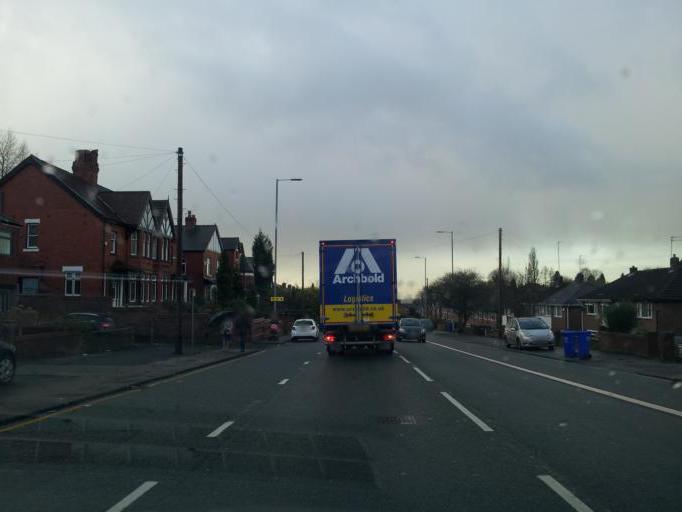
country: GB
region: England
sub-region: Manchester
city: Blackley
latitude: 53.5290
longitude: -2.2110
